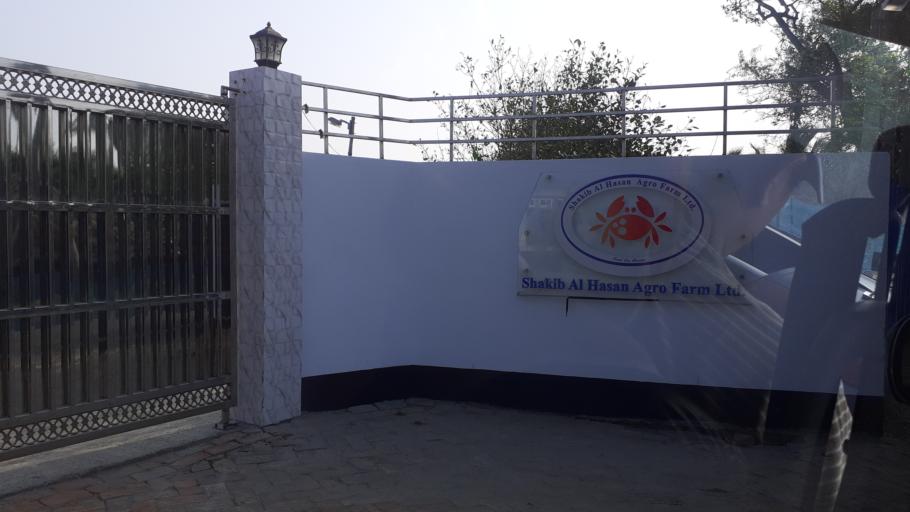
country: IN
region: West Bengal
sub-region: North 24 Parganas
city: Gosaba
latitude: 22.2613
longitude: 89.2244
